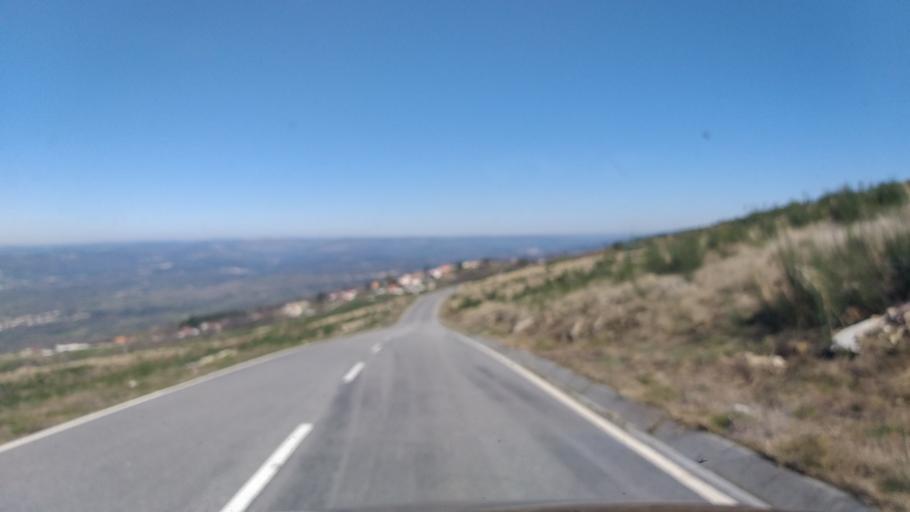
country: PT
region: Guarda
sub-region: Manteigas
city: Manteigas
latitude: 40.4971
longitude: -7.5247
